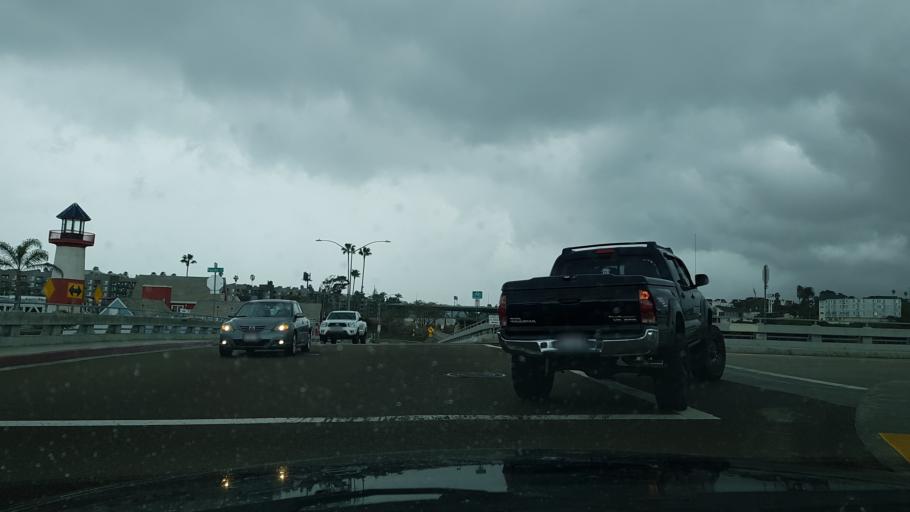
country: US
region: California
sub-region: San Diego County
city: Oceanside
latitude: 33.2040
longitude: -117.3904
